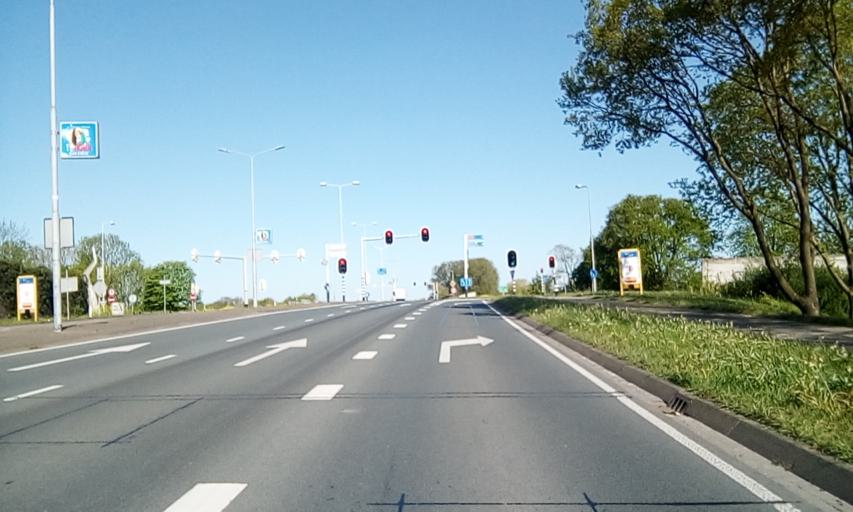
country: NL
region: Gelderland
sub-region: Gemeente Tiel
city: Tiel
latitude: 51.8997
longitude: 5.4340
